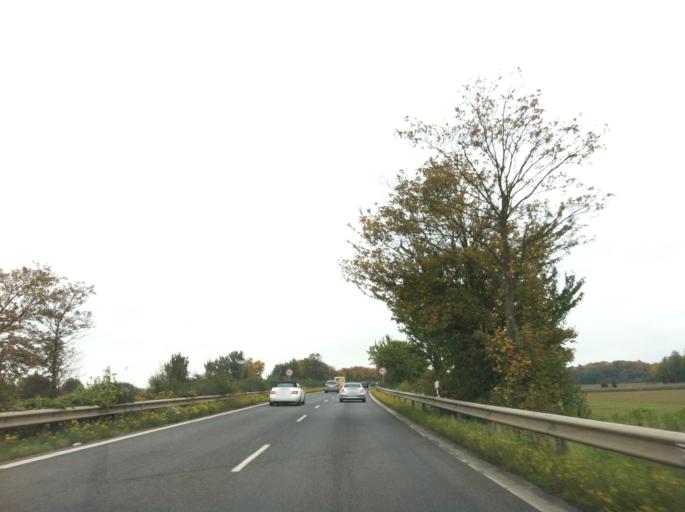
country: DE
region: North Rhine-Westphalia
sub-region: Regierungsbezirk Koln
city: Dueren
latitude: 50.8248
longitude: 6.4814
